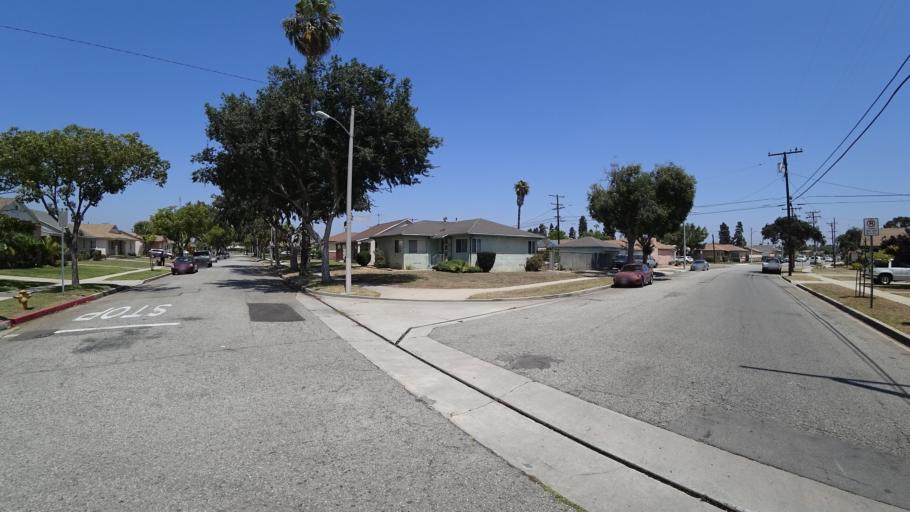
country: US
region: California
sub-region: Los Angeles County
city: West Athens
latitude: 33.9263
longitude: -118.3285
